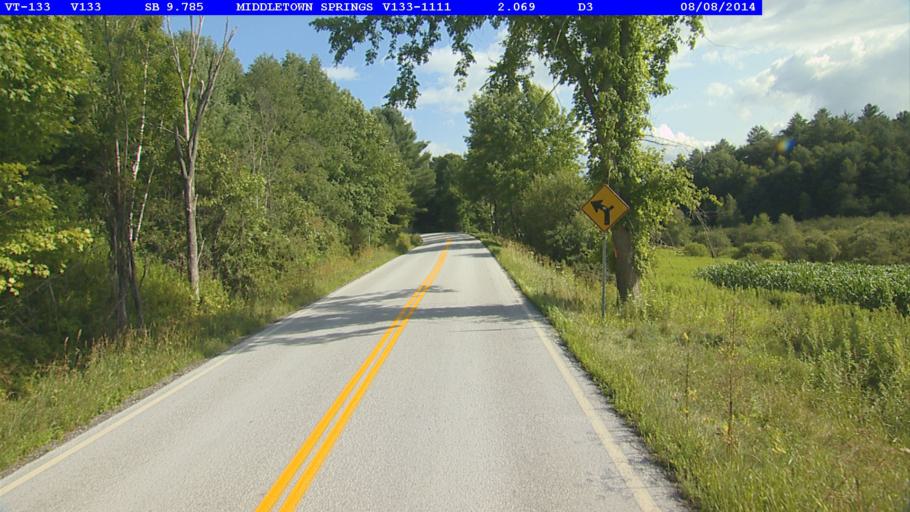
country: US
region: Vermont
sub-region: Rutland County
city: Poultney
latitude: 43.4646
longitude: -73.1131
